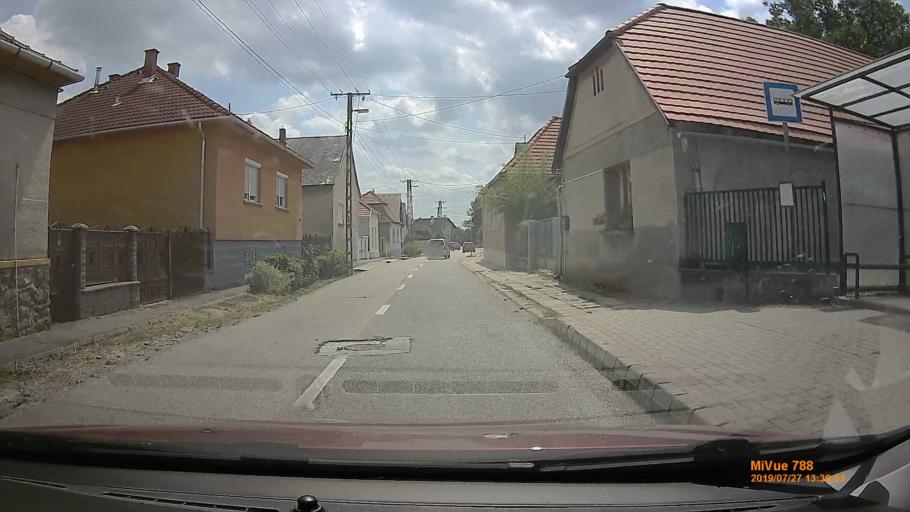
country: HU
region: Veszprem
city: Ajka
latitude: 47.1334
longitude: 17.5690
